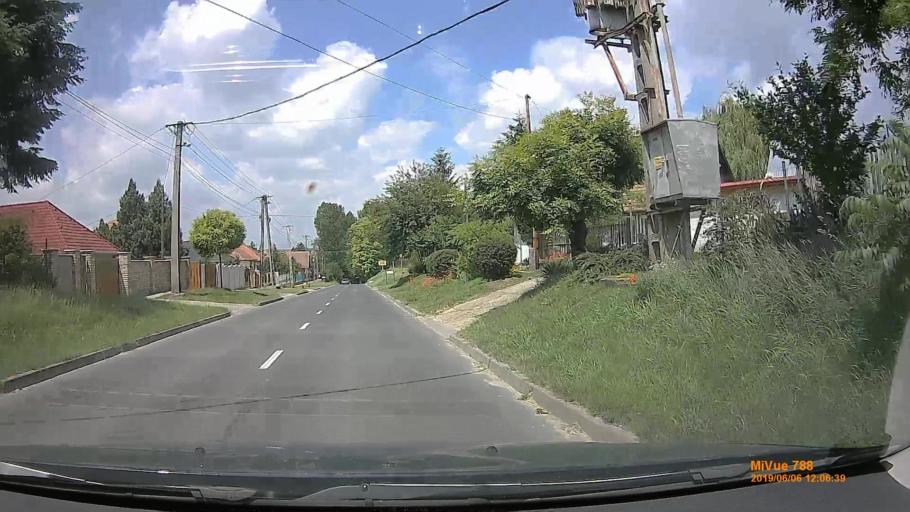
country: HU
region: Pest
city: Kerepes
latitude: 47.5631
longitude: 19.2779
